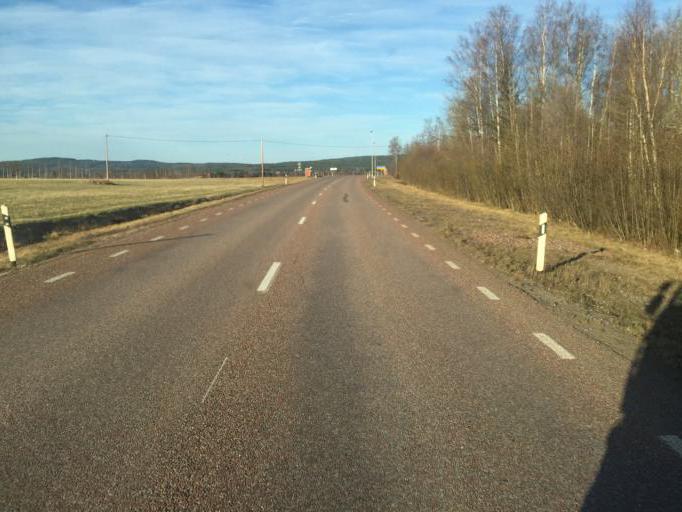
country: SE
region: Dalarna
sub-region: Gagnefs Kommun
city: Gagnef
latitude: 60.5498
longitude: 15.0812
